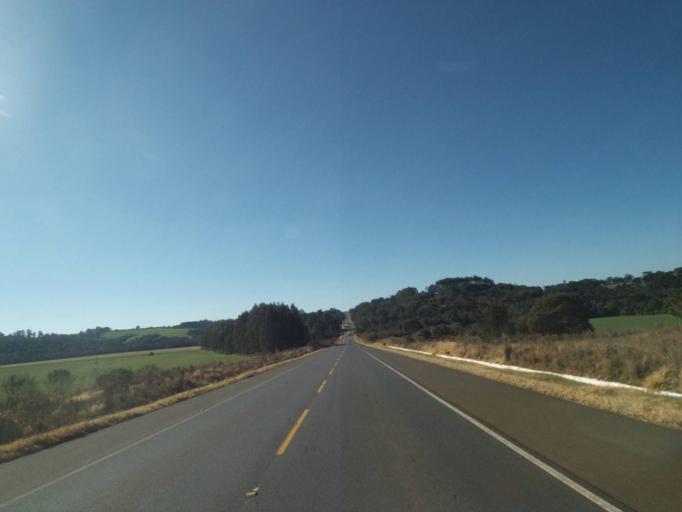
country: BR
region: Parana
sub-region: Tibagi
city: Tibagi
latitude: -24.6146
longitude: -50.4463
